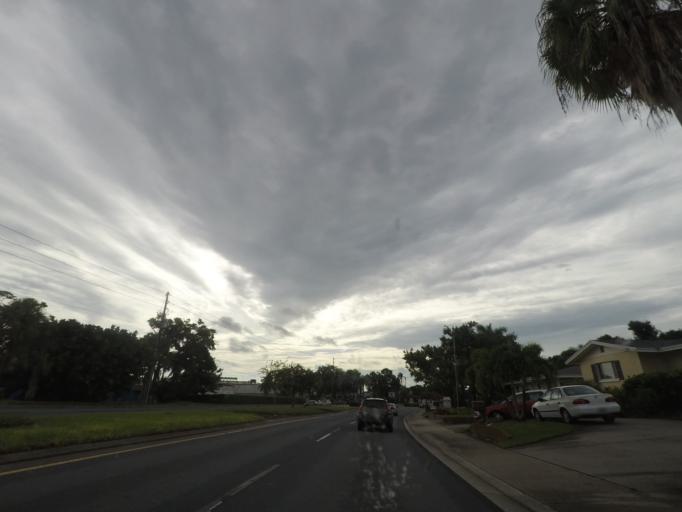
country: US
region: Florida
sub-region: Pinellas County
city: Seminole
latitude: 27.8433
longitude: -82.7983
